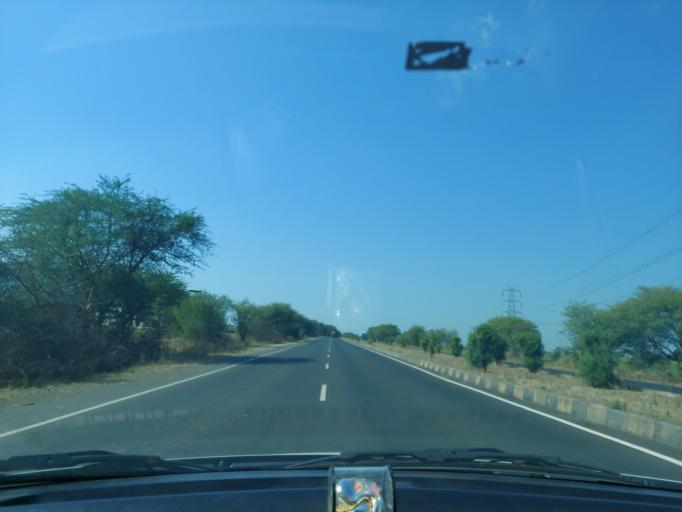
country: IN
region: Madhya Pradesh
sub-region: Indore
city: Manpur
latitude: 22.5014
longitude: 75.5560
